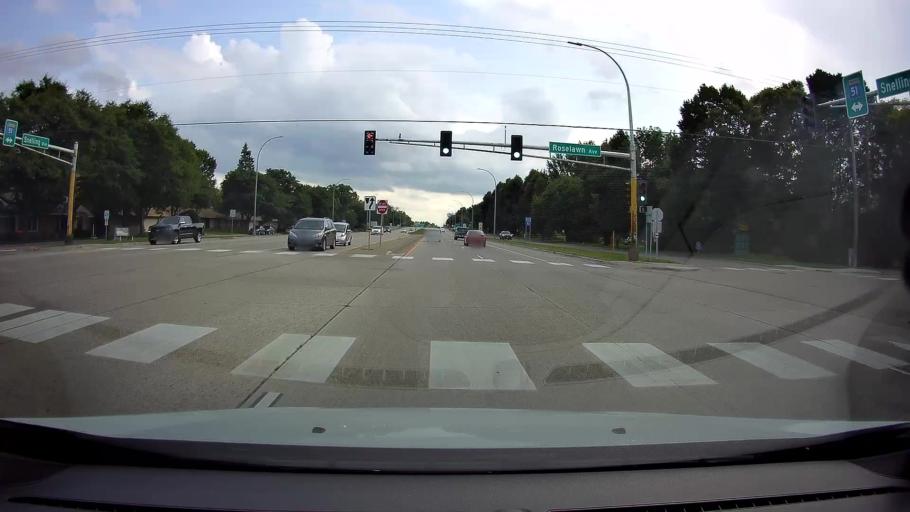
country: US
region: Minnesota
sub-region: Ramsey County
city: Falcon Heights
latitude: 44.9991
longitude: -93.1666
